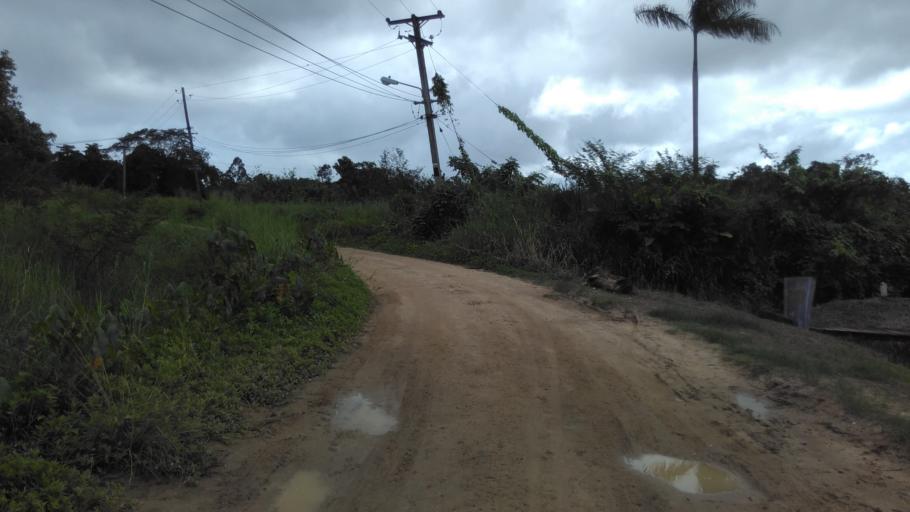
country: SR
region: Paramaribo
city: Paramaribo
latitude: 5.7735
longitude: -55.1314
